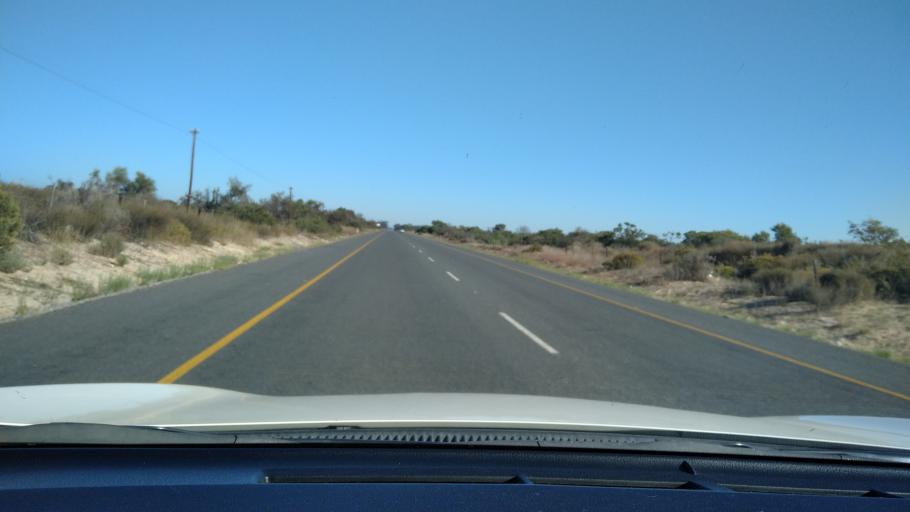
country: ZA
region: Western Cape
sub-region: West Coast District Municipality
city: Moorreesburg
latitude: -33.0772
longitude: 18.3832
